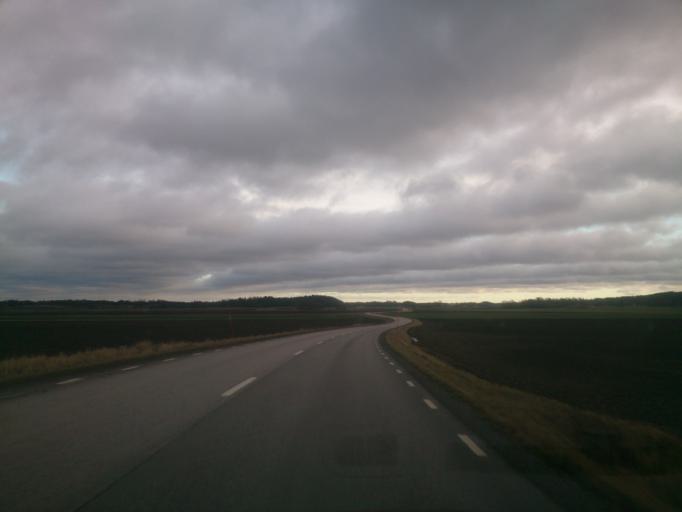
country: SE
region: OEstergoetland
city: Lindo
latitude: 58.5813
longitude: 16.3255
